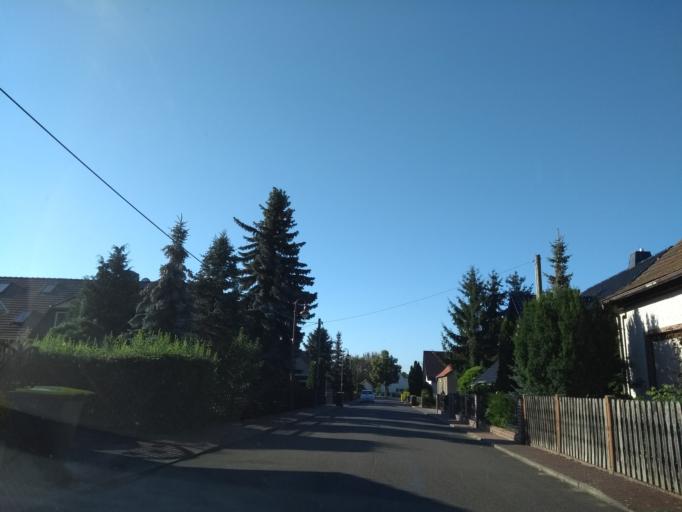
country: DE
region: Brandenburg
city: Lubbenau
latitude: 51.8376
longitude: 13.9521
